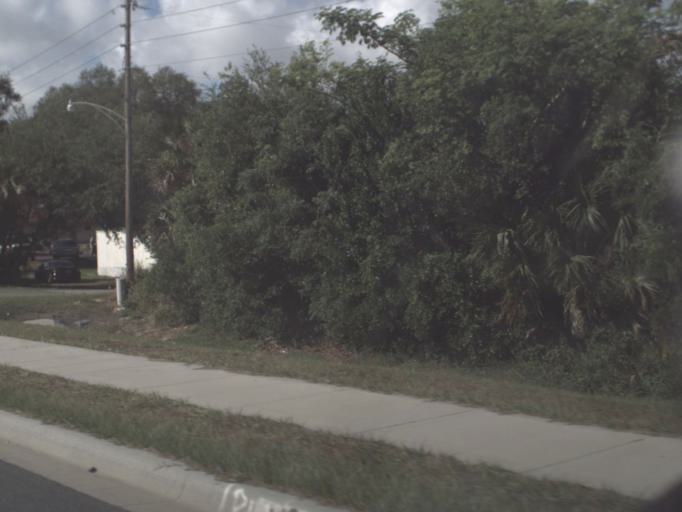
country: US
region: Florida
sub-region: Lake County
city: Fruitland Park
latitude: 28.8475
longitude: -81.8995
